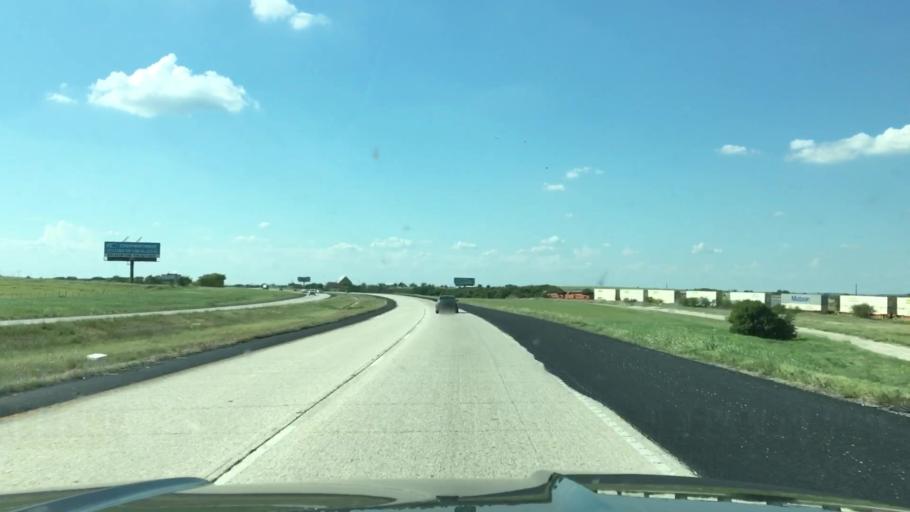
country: US
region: Texas
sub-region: Wise County
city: New Fairview
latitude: 33.1443
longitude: -97.5000
